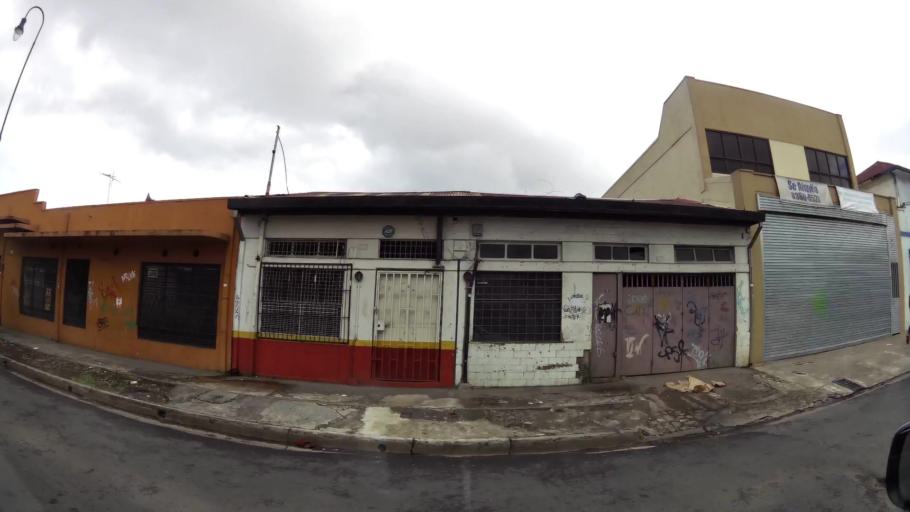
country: CR
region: San Jose
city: San Jose
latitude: 9.9266
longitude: -84.0750
